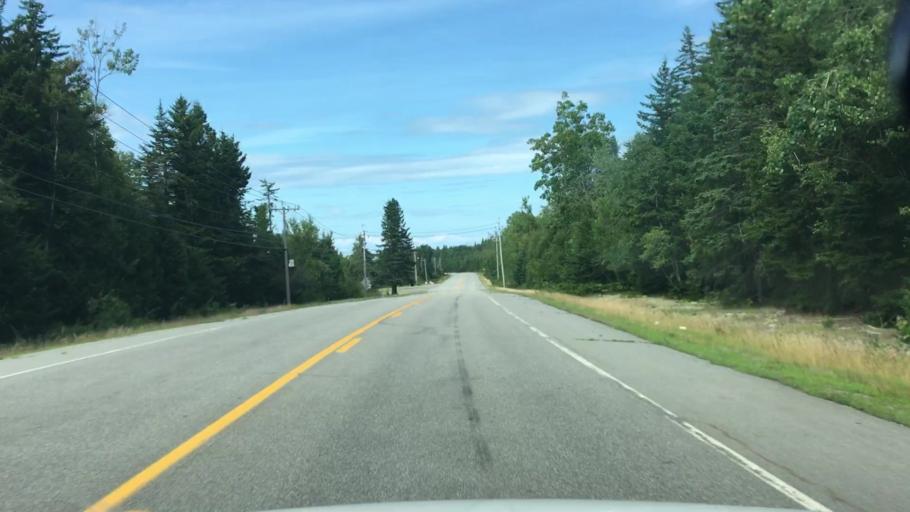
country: US
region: Maine
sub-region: Washington County
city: Eastport
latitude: 44.9304
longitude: -67.0263
